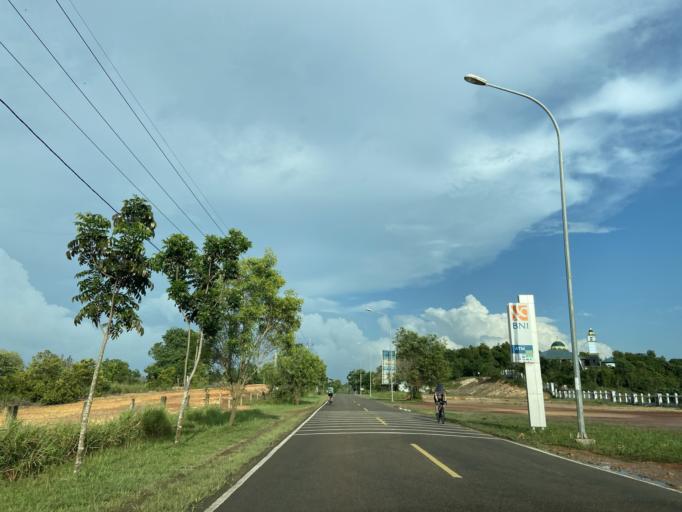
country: ID
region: Riau Islands
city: Tanjungpinang
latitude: 0.9512
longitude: 104.0716
